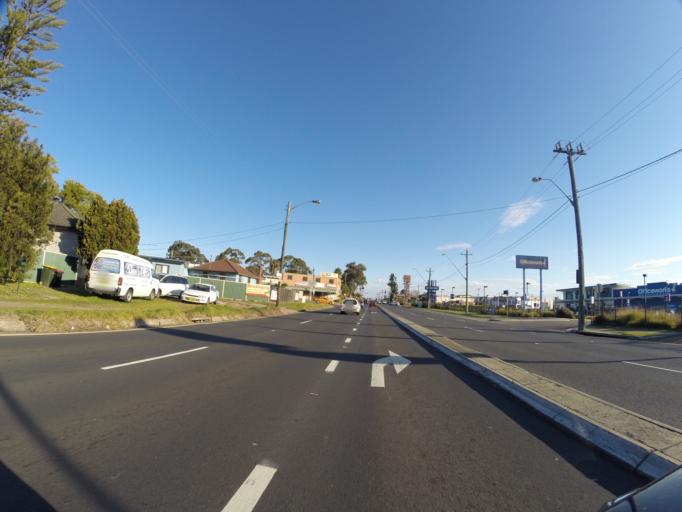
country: AU
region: New South Wales
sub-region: Fairfield
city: Fairfield East
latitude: -33.8696
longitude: 150.9862
